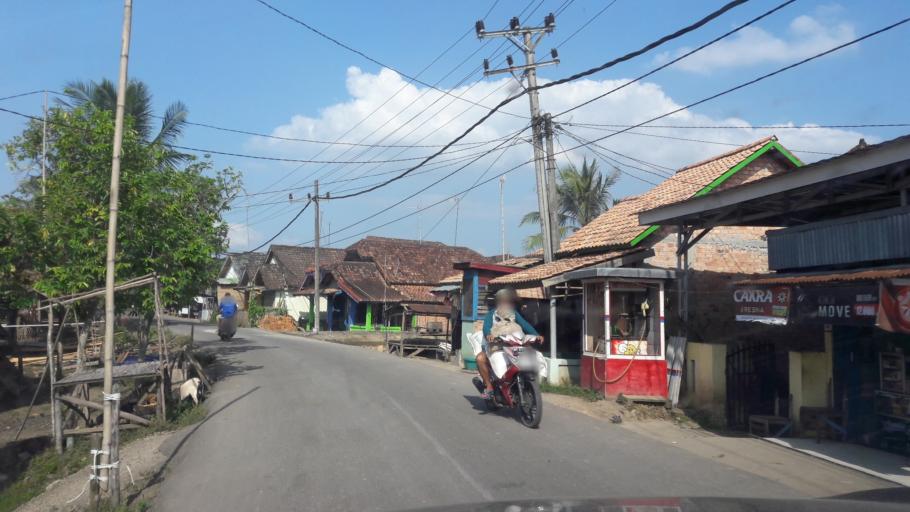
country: ID
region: South Sumatra
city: Prabumulih
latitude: -3.2809
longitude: 104.2310
